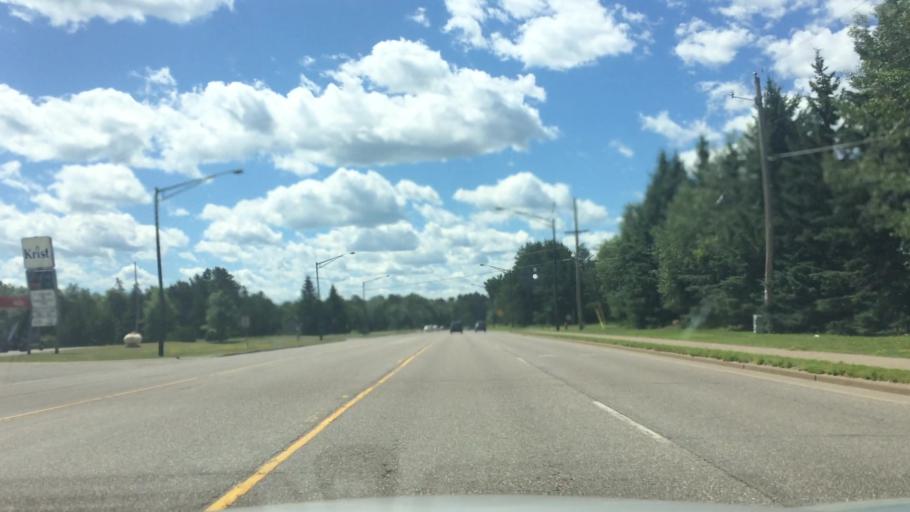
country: US
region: Wisconsin
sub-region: Vilas County
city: Lac du Flambeau
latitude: 45.8848
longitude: -89.7292
